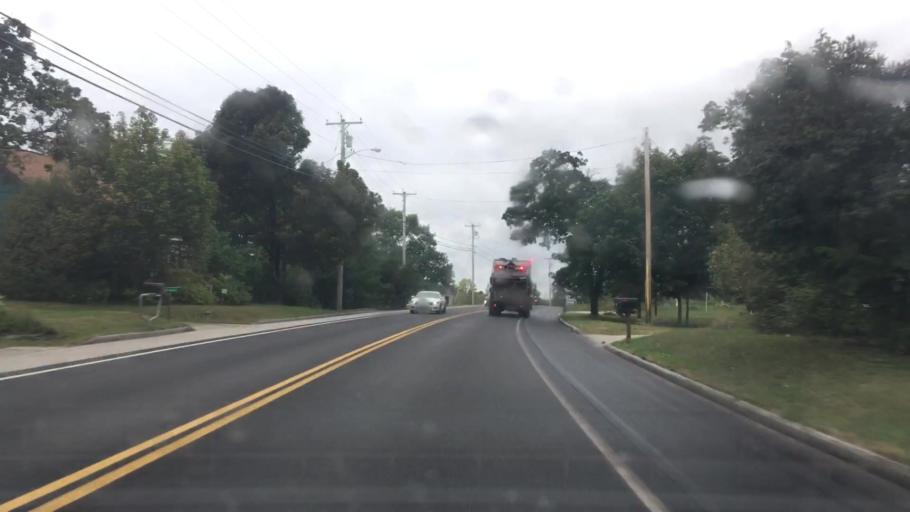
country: US
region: Maine
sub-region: Penobscot County
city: Orrington
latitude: 44.7466
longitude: -68.8076
